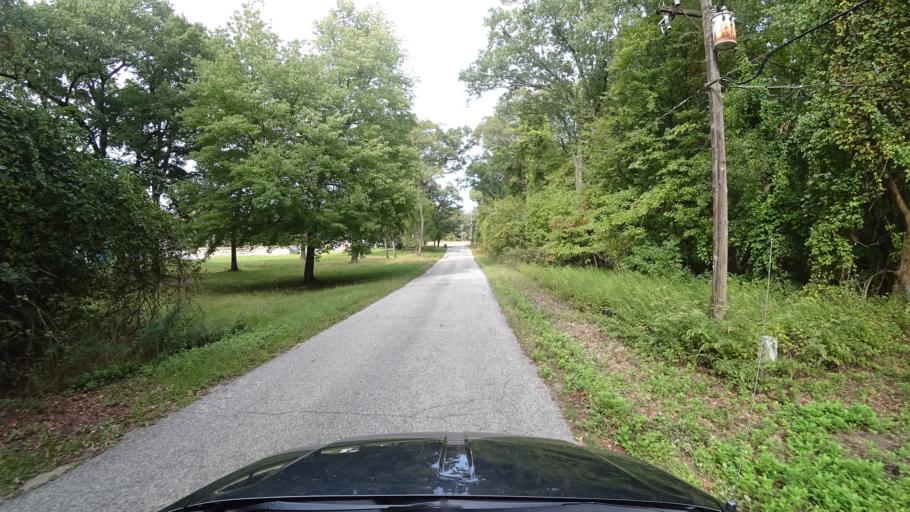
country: US
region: Indiana
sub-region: LaPorte County
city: Long Beach
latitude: 41.7363
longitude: -86.8458
